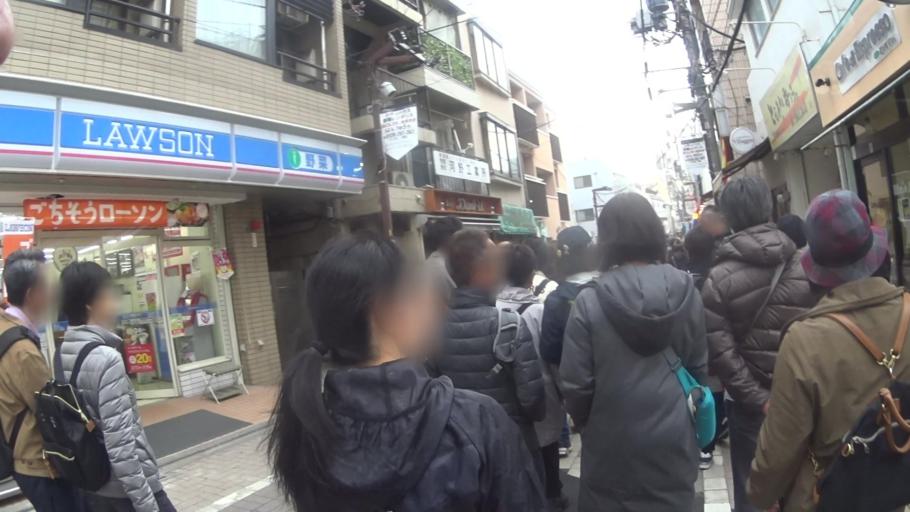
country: JP
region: Tokyo
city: Tokyo
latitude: 35.6797
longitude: 139.6770
